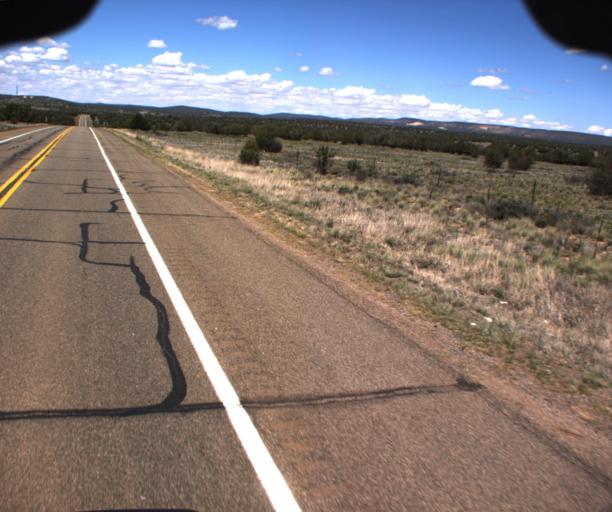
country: US
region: Arizona
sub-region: Coconino County
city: Williams
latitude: 35.1937
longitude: -112.4710
